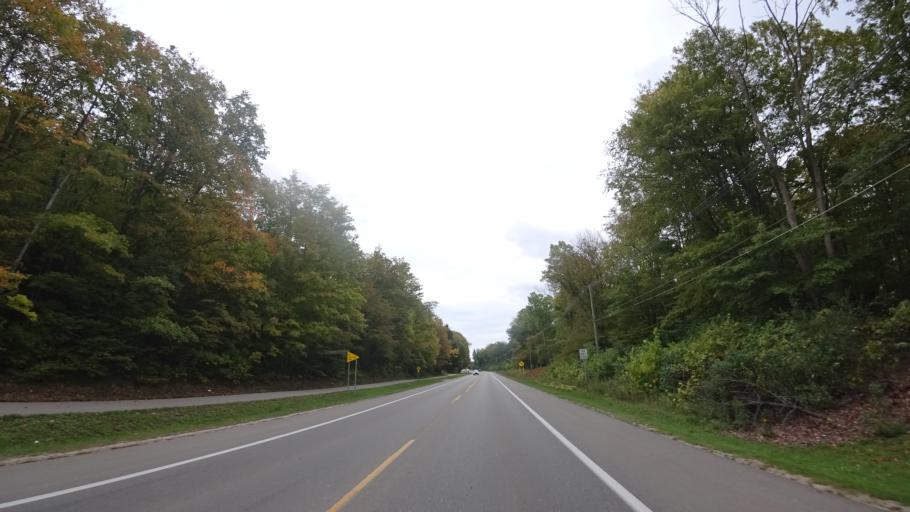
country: US
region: Michigan
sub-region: Emmet County
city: Petoskey
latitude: 45.4287
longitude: -84.9214
